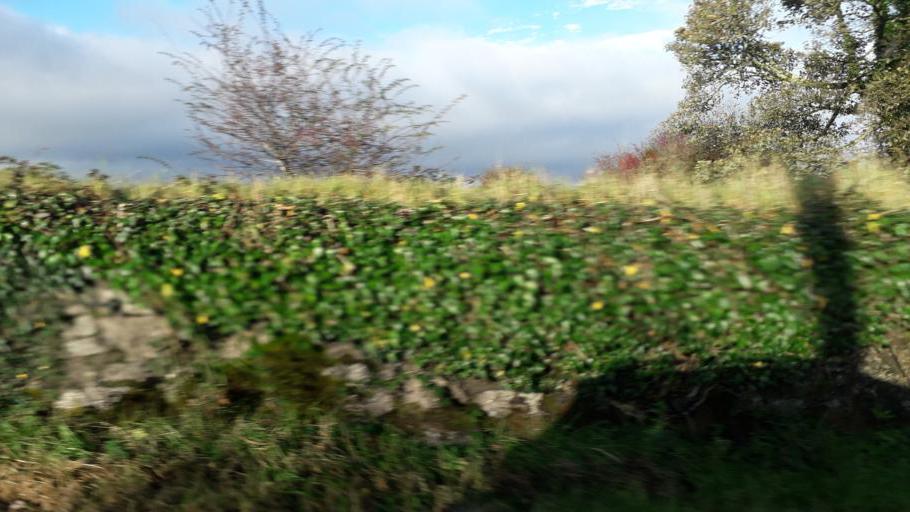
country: IE
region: Connaught
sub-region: Roscommon
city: Castlerea
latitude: 53.8730
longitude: -8.4196
